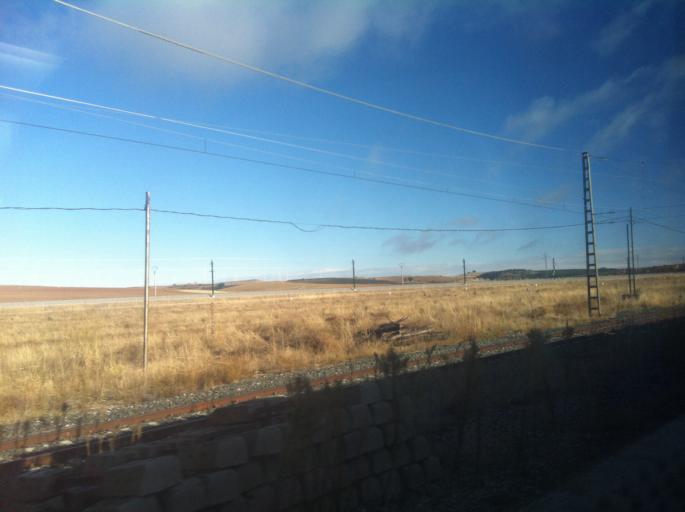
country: ES
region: Castille and Leon
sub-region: Provincia de Palencia
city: Villodrigo
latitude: 42.1465
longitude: -4.1071
